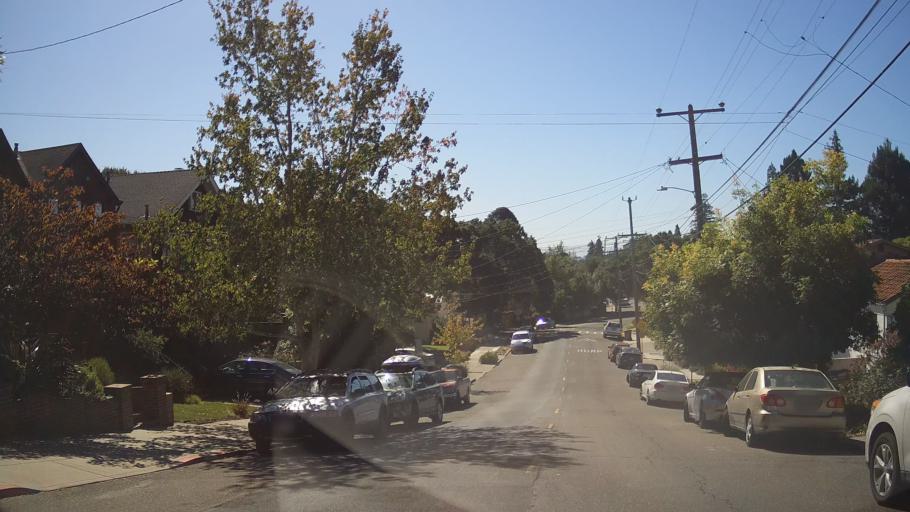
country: US
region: California
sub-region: Alameda County
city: Berkeley
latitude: 37.8855
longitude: -122.2677
